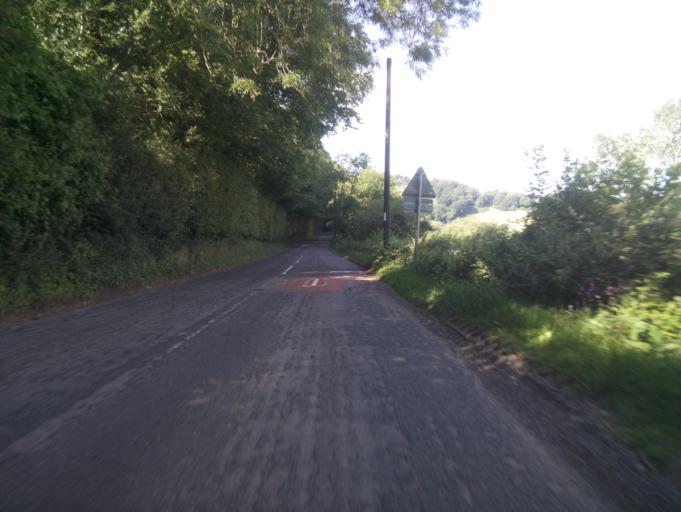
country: GB
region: England
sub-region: Herefordshire
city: Walford
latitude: 51.8740
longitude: -2.6030
